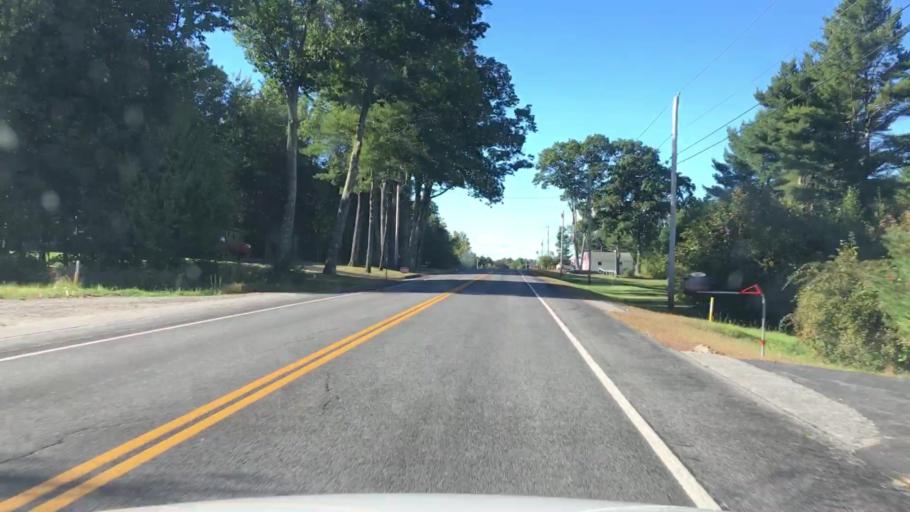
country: US
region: Maine
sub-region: Androscoggin County
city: Lisbon
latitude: 44.0532
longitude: -70.0833
